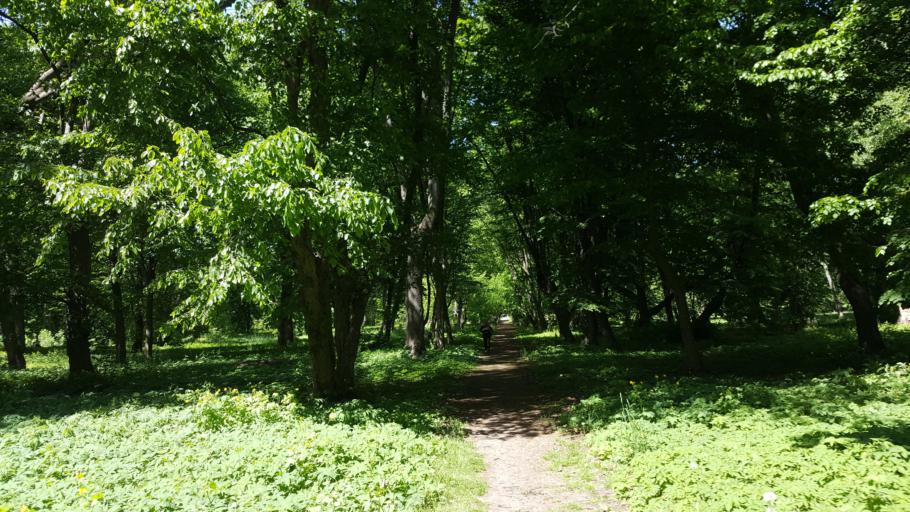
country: BY
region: Brest
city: Brest
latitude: 52.1535
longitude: 23.6392
